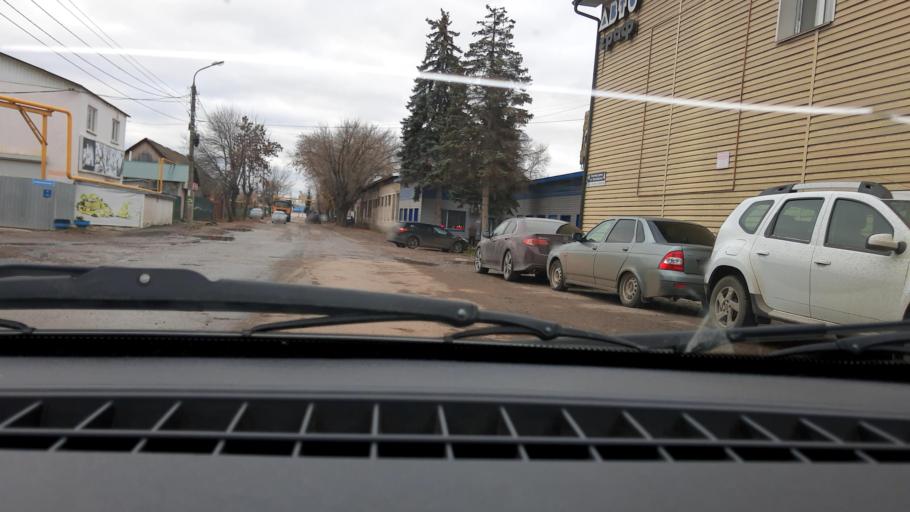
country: RU
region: Bashkortostan
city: Mikhaylovka
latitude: 54.7380
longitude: 55.8982
